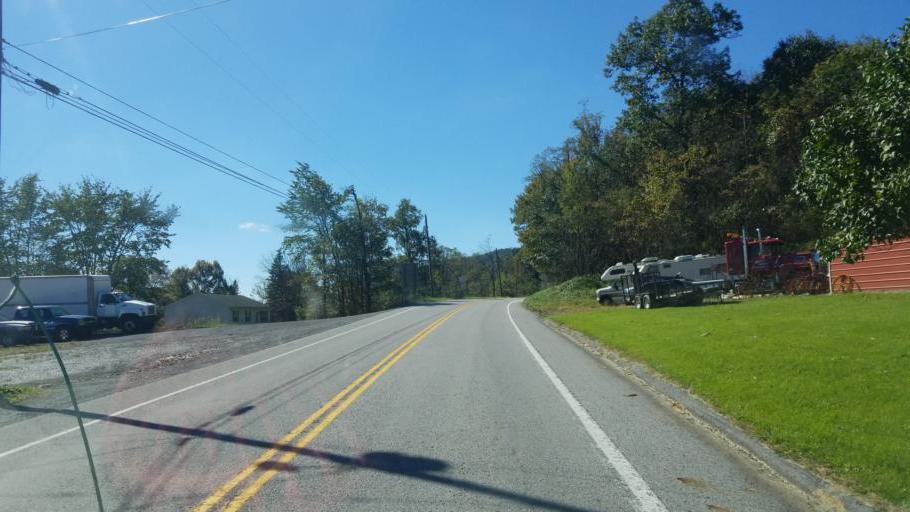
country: US
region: Pennsylvania
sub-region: Somerset County
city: Central City
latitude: 40.0433
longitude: -78.7482
